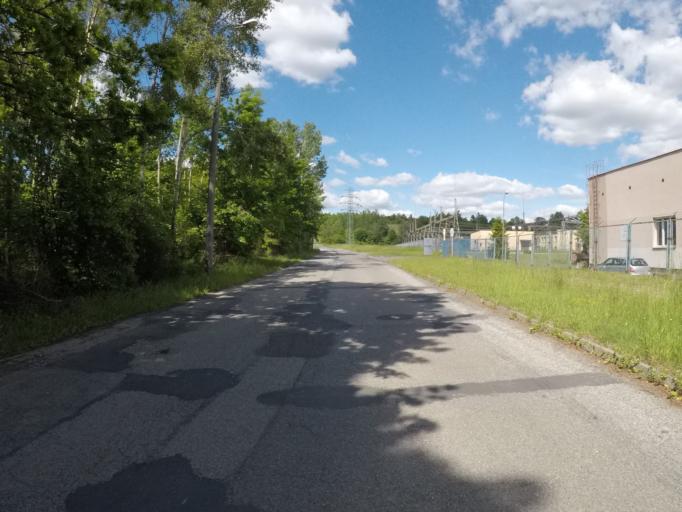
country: PL
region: Swietokrzyskie
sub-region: Powiat kielecki
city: Kostomloty Pierwsze
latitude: 50.8990
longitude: 20.6116
